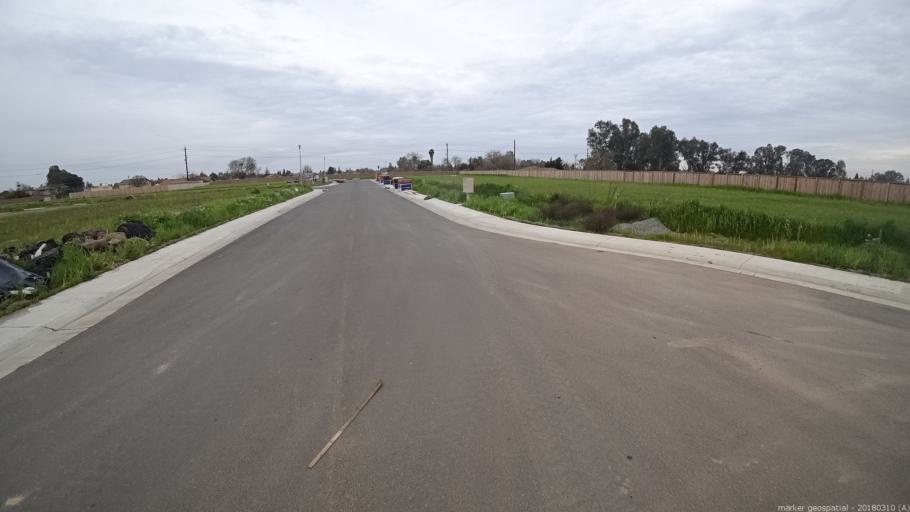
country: US
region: California
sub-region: Sacramento County
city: Florin
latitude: 38.4738
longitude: -121.3829
